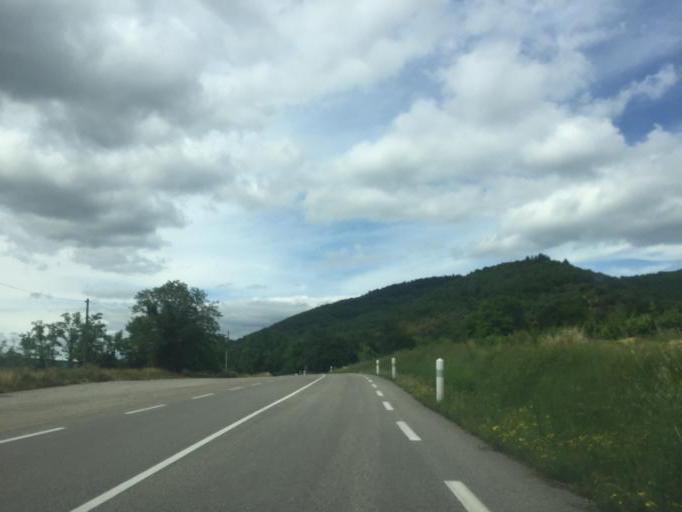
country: FR
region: Rhone-Alpes
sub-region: Departement de l'Ardeche
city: Alba-la-Romaine
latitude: 44.5359
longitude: 4.6152
